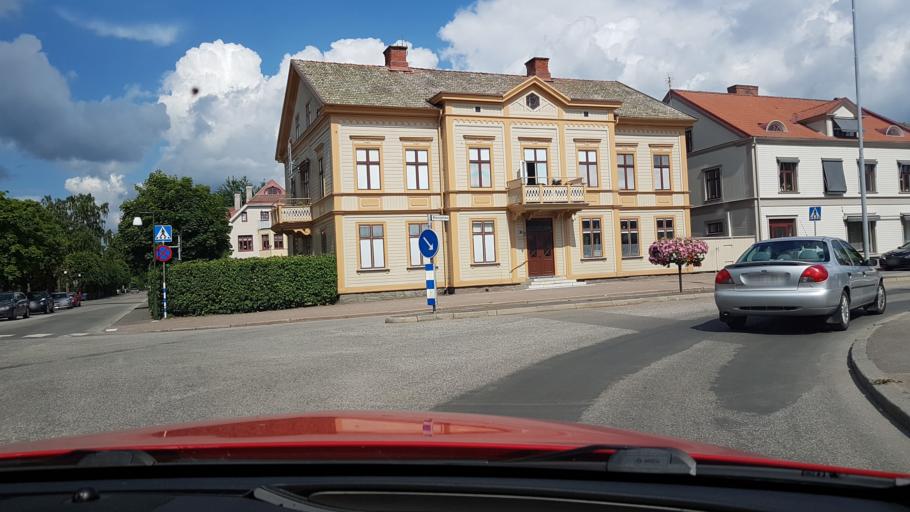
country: SE
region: Vaestra Goetaland
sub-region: Hjo Kommun
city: Hjo
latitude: 58.3037
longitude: 14.2913
